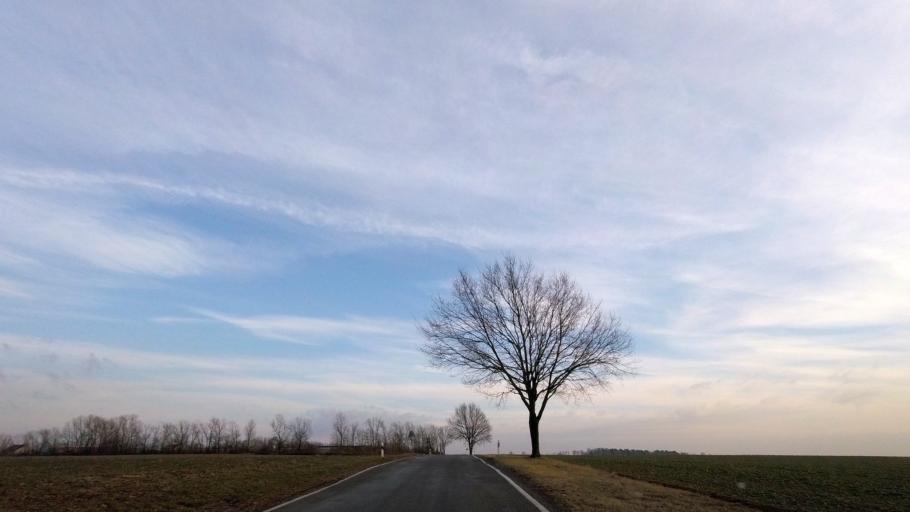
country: DE
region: Brandenburg
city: Wiesenburg
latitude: 52.1173
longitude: 12.5237
